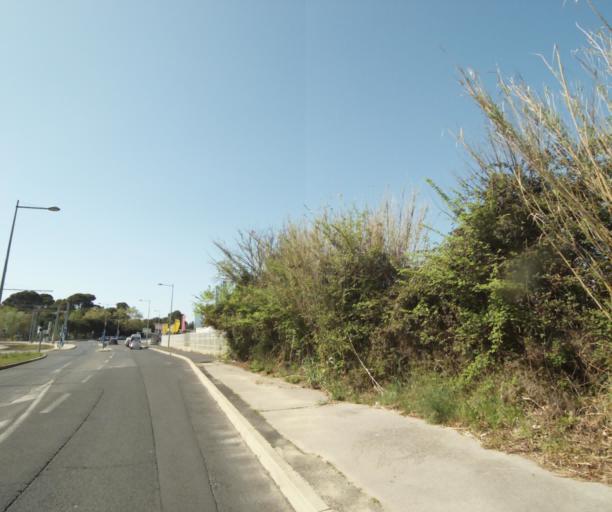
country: FR
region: Languedoc-Roussillon
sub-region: Departement de l'Herault
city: Juvignac
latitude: 43.6388
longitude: 3.8297
